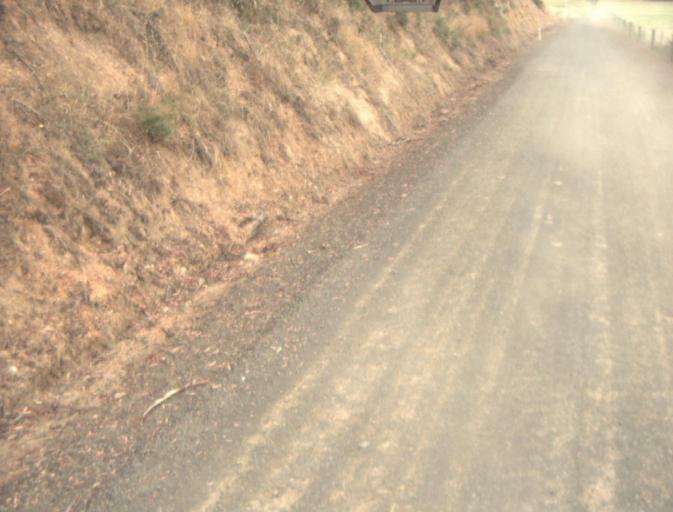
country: AU
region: Tasmania
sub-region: Northern Midlands
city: Evandale
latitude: -41.4685
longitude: 147.5355
